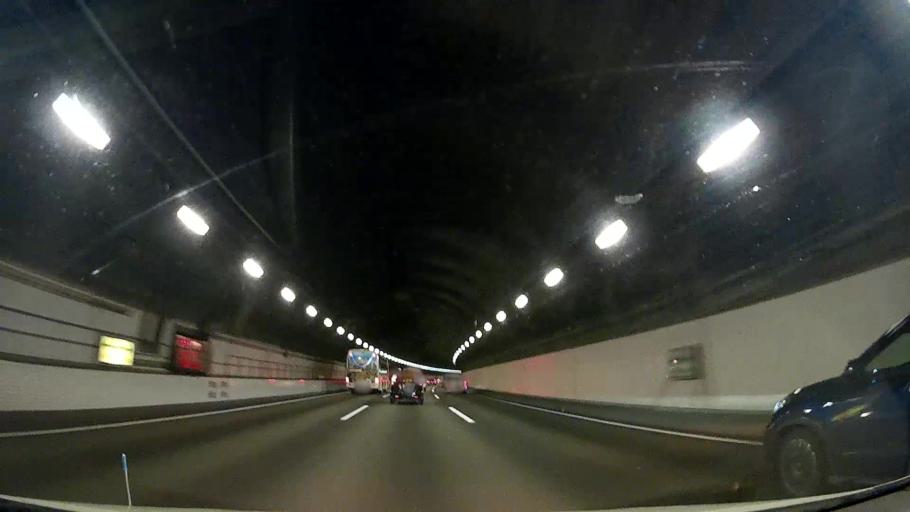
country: JP
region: Shizuoka
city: Gotemba
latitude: 35.3636
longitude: 139.0510
